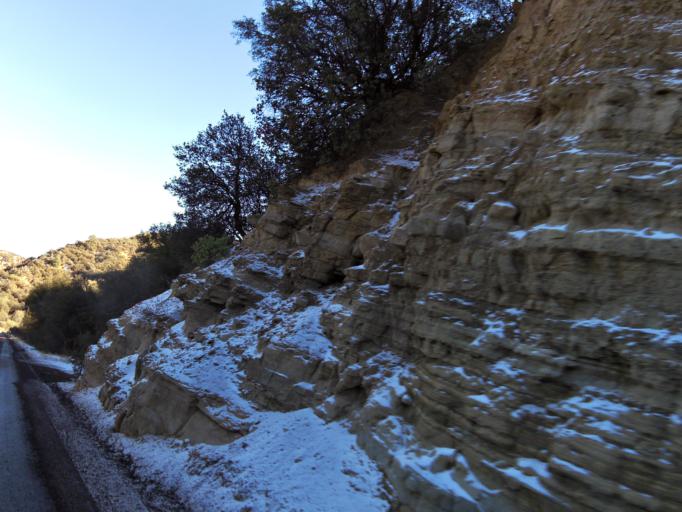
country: US
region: California
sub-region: Ventura County
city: Meiners Oaks
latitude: 34.6781
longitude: -119.3684
